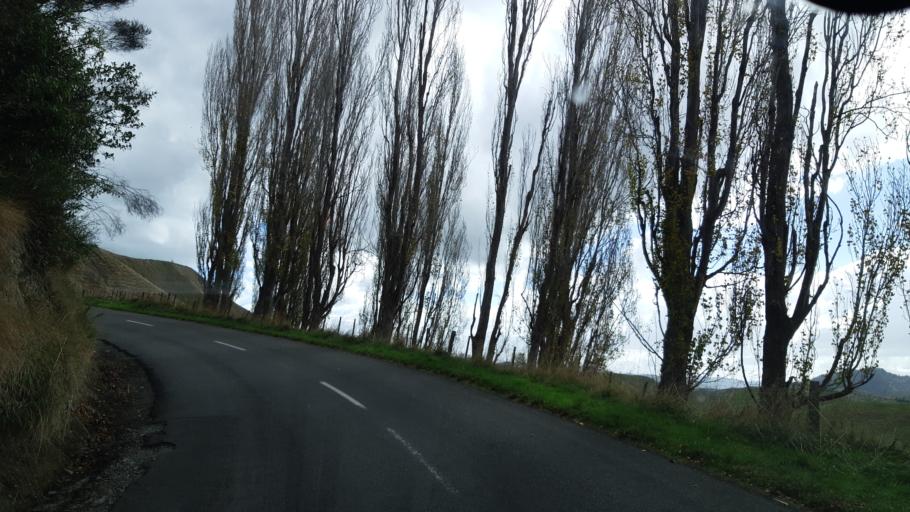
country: NZ
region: Manawatu-Wanganui
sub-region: Rangitikei District
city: Bulls
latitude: -39.9045
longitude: 175.5189
